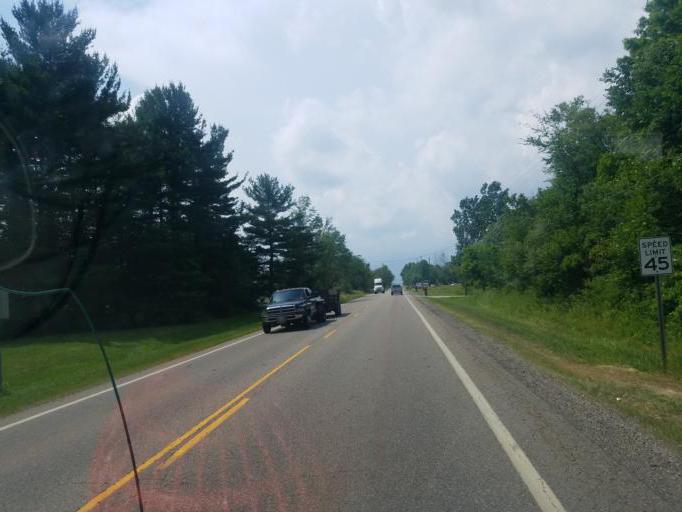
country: US
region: Ohio
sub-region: Portage County
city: Ravenna
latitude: 41.0928
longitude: -81.1391
